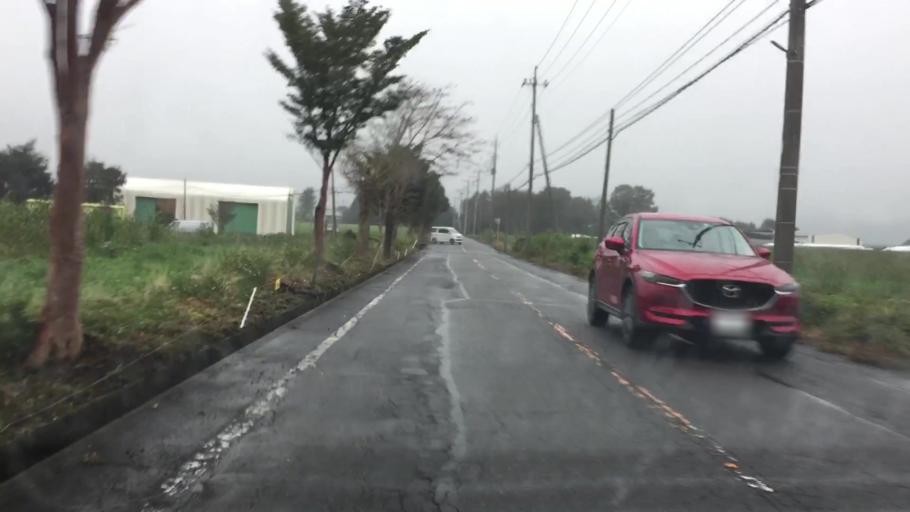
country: JP
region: Yamanashi
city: Fujikawaguchiko
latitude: 35.3907
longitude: 138.5818
